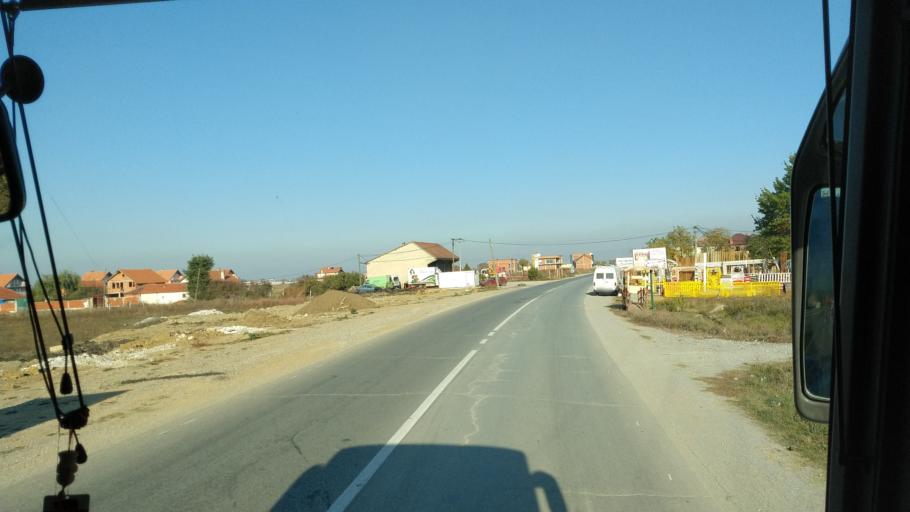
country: XK
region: Ferizaj
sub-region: Komuna e Shtimes
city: Shtime
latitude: 42.4486
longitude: 21.0637
